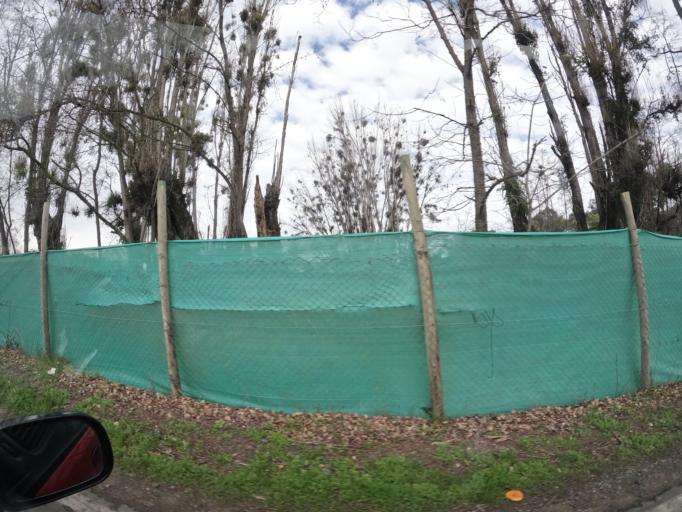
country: CL
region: Maule
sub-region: Provincia de Linares
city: Linares
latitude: -35.8664
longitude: -71.6274
